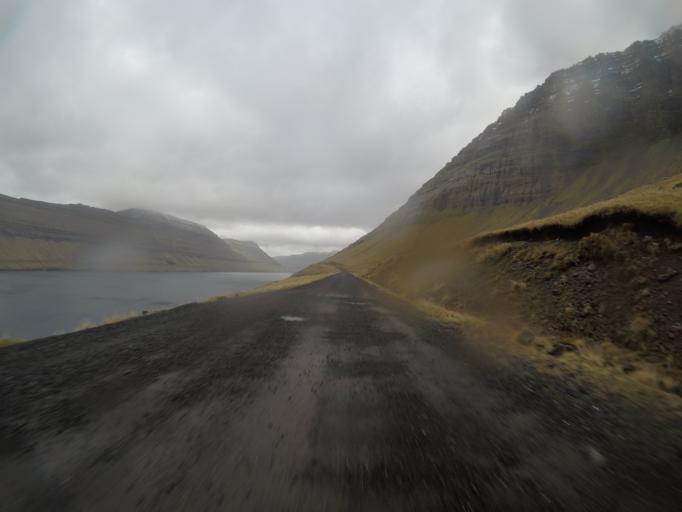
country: FO
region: Nordoyar
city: Klaksvik
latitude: 62.3350
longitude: -6.5771
